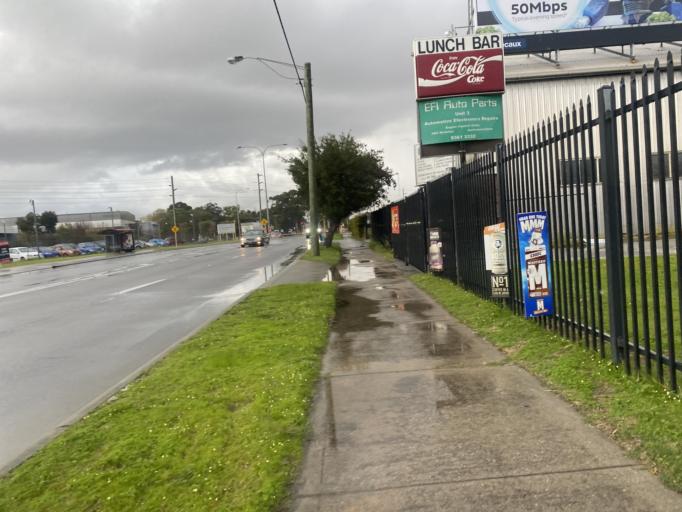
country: AU
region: Western Australia
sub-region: Canning
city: Bentley
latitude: -31.9941
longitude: 115.9200
